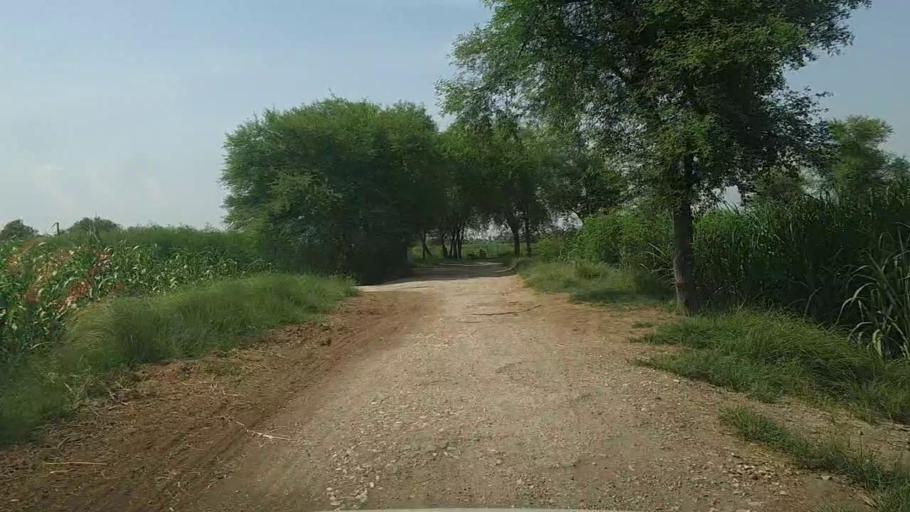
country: PK
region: Sindh
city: Ubauro
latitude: 28.1760
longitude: 69.8144
